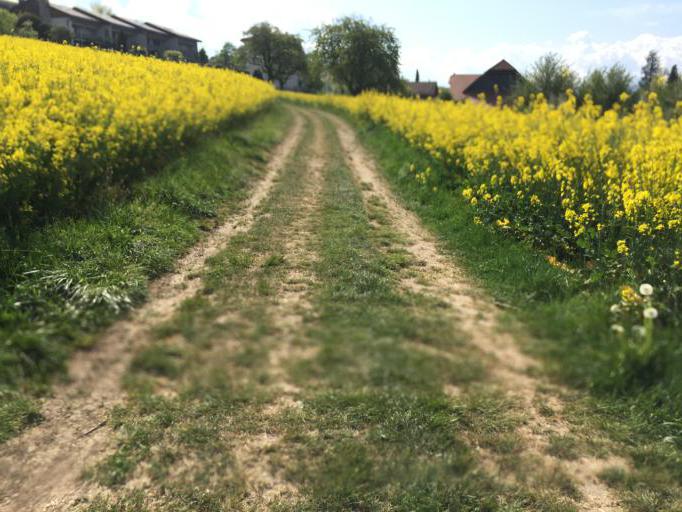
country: CH
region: Bern
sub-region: Bern-Mittelland District
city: Munsingen
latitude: 46.8828
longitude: 7.5661
